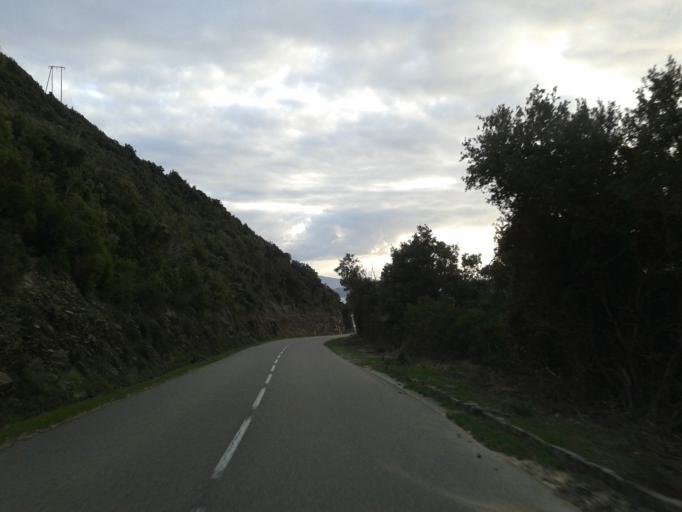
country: FR
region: Corsica
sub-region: Departement de la Haute-Corse
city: Santa-Maria-di-Lota
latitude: 42.7691
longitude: 9.3429
